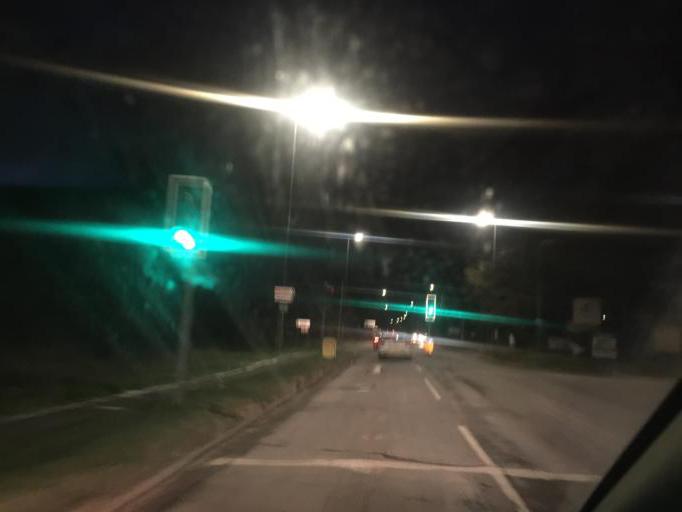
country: GB
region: England
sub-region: Royal Borough of Windsor and Maidenhead
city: Bray
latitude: 51.5221
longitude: -0.6799
